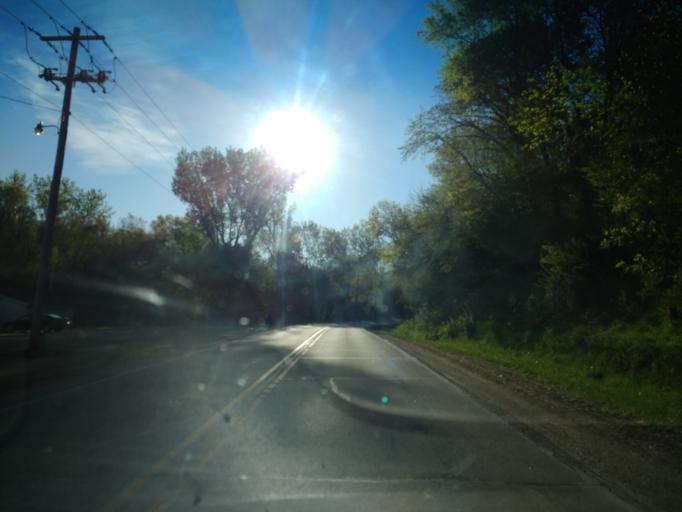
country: US
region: Iowa
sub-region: Harrison County
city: Missouri Valley
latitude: 41.4326
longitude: -95.8617
